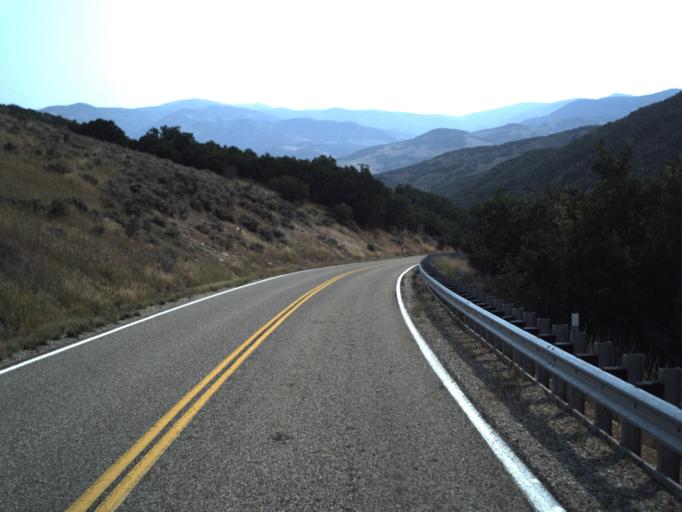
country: US
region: Utah
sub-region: Summit County
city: Summit Park
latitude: 40.8538
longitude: -111.6113
